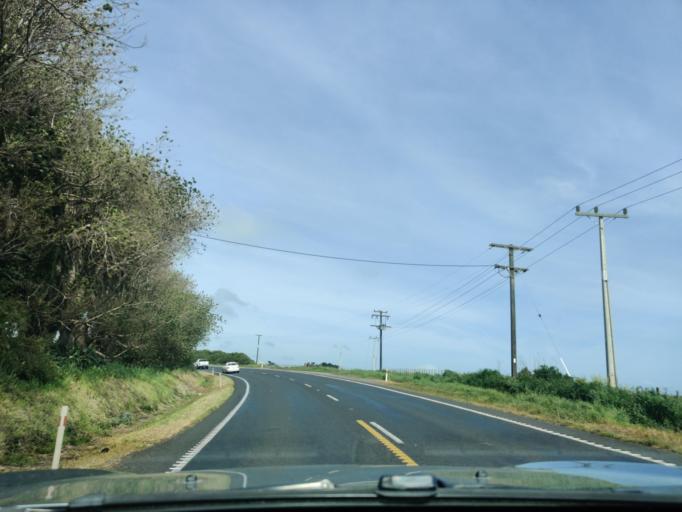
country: NZ
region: Taranaki
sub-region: South Taranaki District
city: Hawera
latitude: -39.6499
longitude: 174.3852
